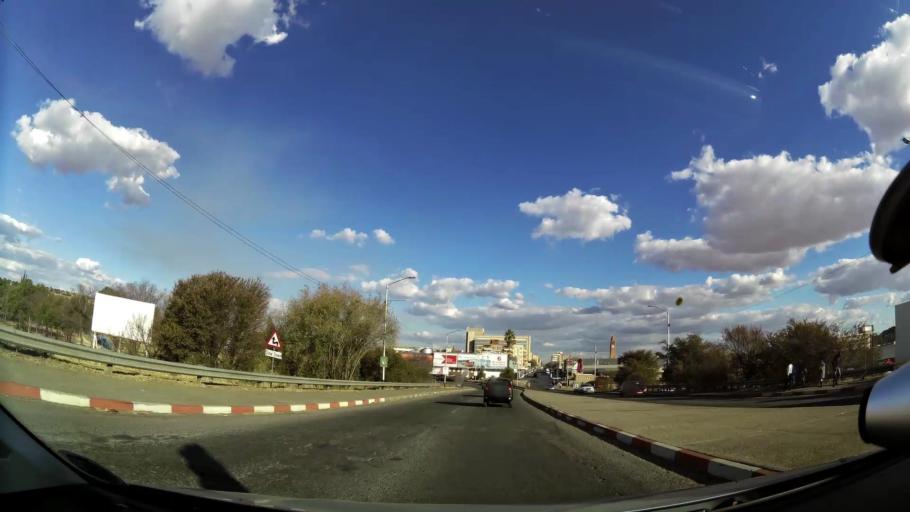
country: ZA
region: North-West
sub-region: Dr Kenneth Kaunda District Municipality
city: Klerksdorp
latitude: -26.8617
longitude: 26.6656
